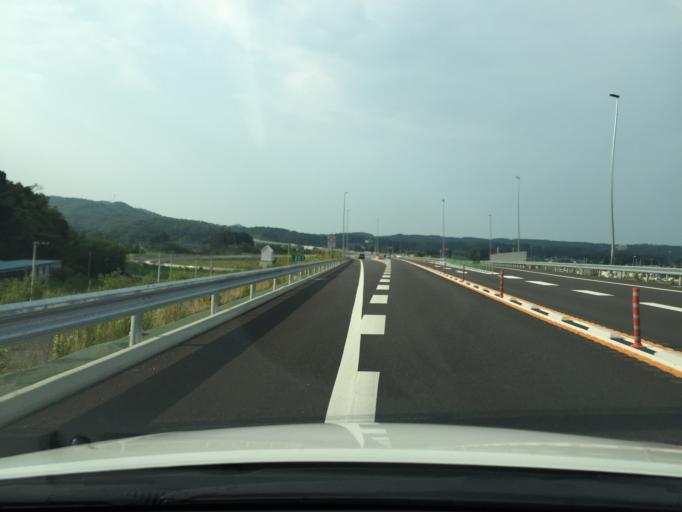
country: JP
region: Fukushima
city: Namie
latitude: 37.6555
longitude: 140.9190
